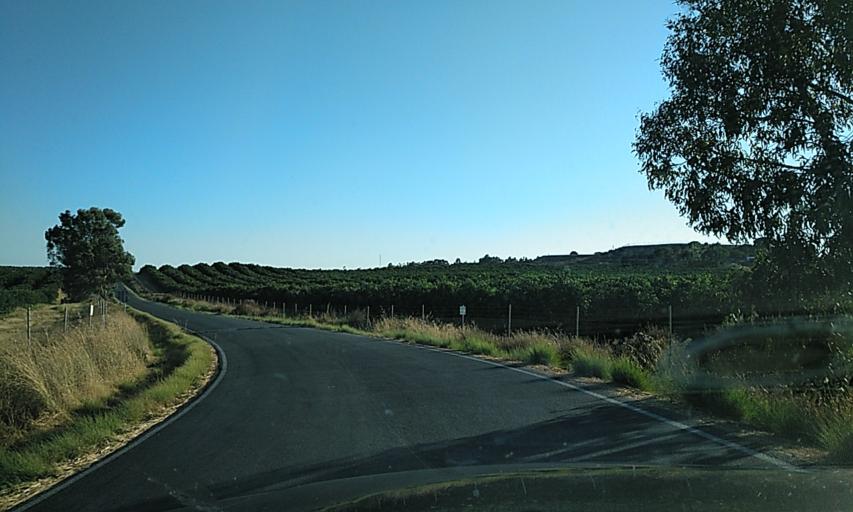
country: ES
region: Andalusia
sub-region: Provincia de Huelva
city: San Bartolome de la Torre
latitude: 37.4138
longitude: -7.1196
